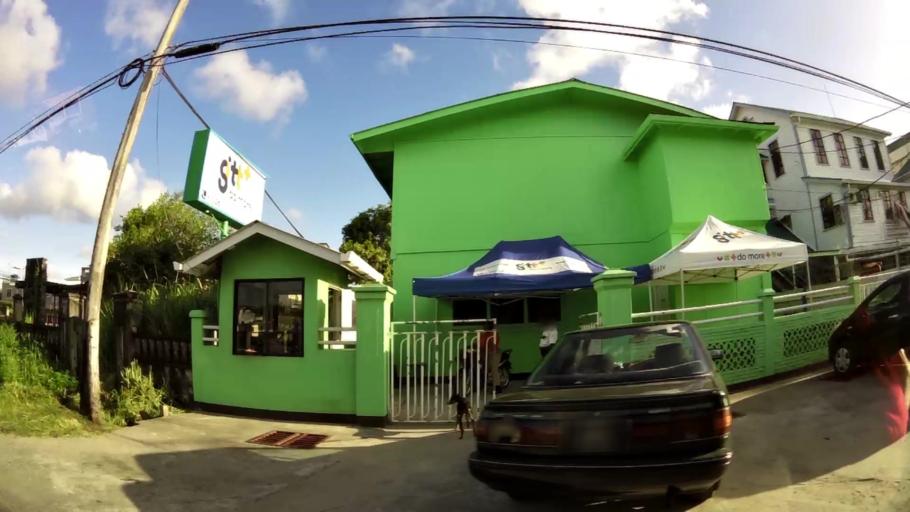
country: GY
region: Demerara-Mahaica
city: Georgetown
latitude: 6.8077
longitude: -58.1584
